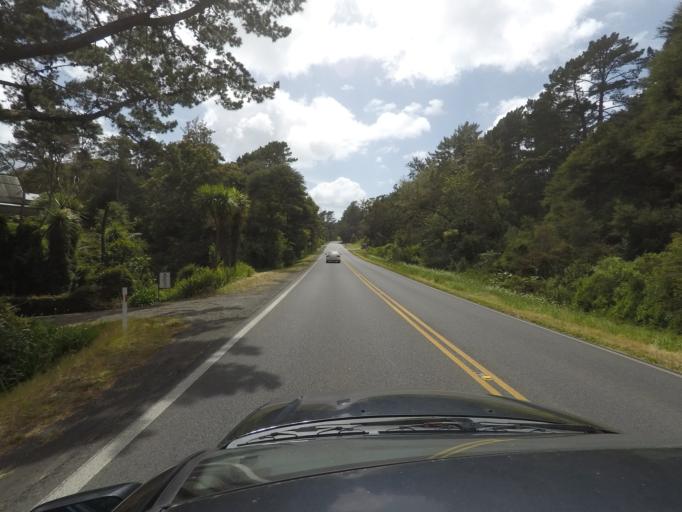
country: NZ
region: Auckland
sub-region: Auckland
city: Warkworth
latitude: -36.5580
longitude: 174.6986
